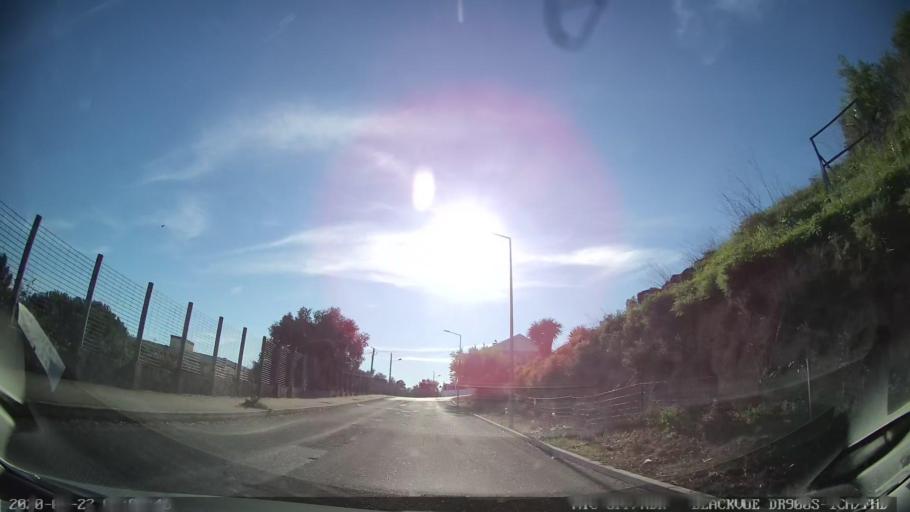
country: PT
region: Lisbon
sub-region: Vila Franca de Xira
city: Vila Franca de Xira
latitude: 38.9593
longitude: -8.9914
